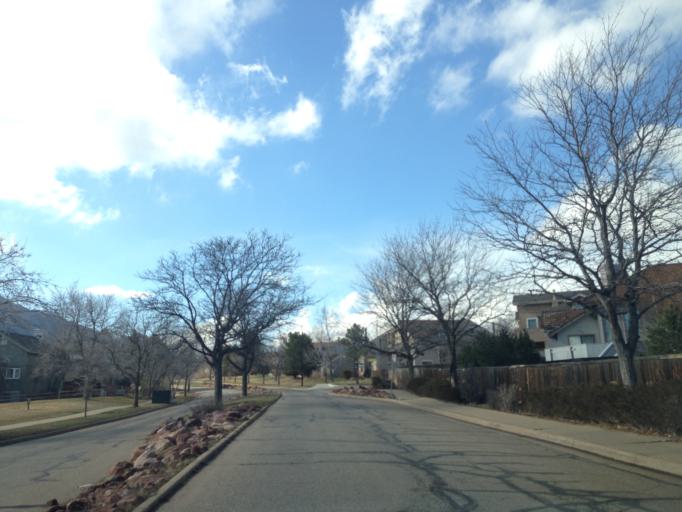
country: US
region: Colorado
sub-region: Boulder County
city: Boulder
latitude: 39.9653
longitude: -105.2544
